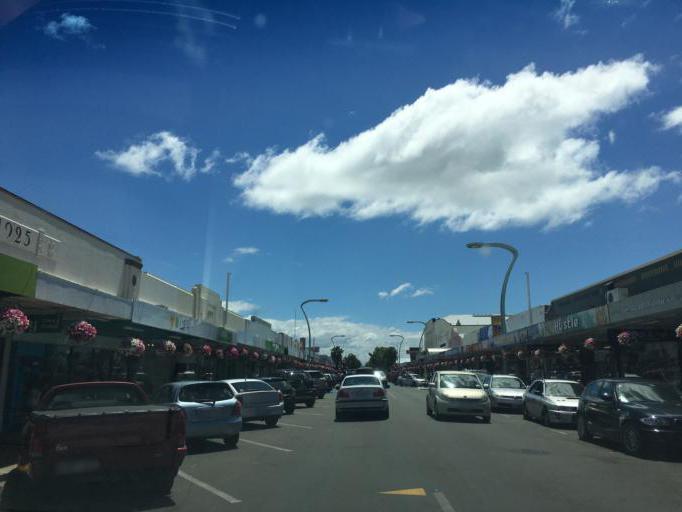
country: NZ
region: Hawke's Bay
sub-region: Hastings District
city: Hastings
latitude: -39.6400
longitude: 176.8412
